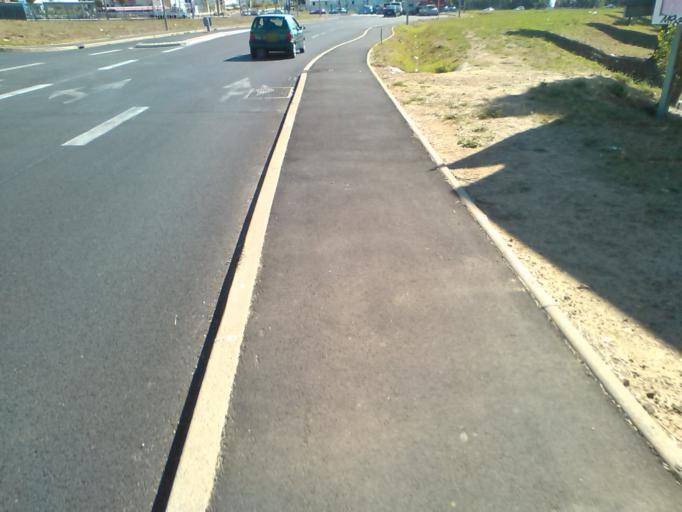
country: FR
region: Languedoc-Roussillon
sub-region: Departement de l'Herault
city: Perols
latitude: 43.5773
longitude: 3.9342
